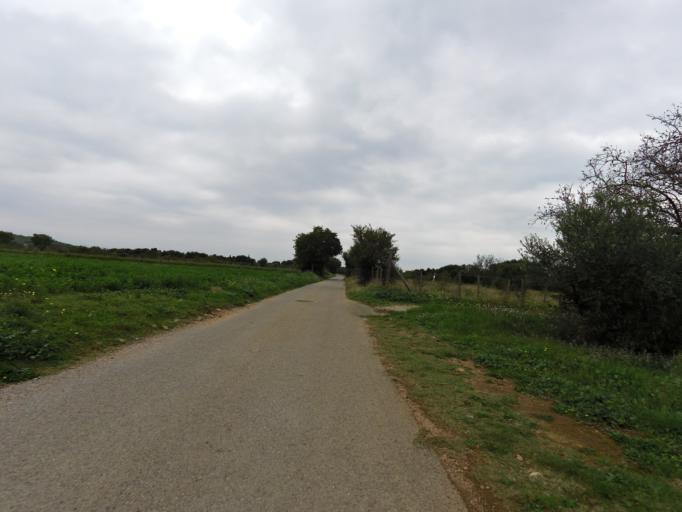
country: FR
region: Languedoc-Roussillon
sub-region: Departement de l'Herault
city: Villetelle
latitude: 43.7274
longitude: 4.1442
